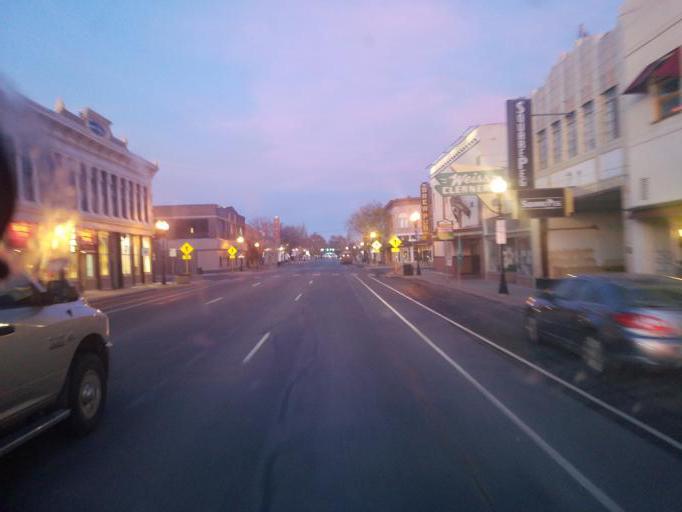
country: US
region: Colorado
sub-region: Alamosa County
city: Alamosa
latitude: 37.4683
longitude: -105.8664
